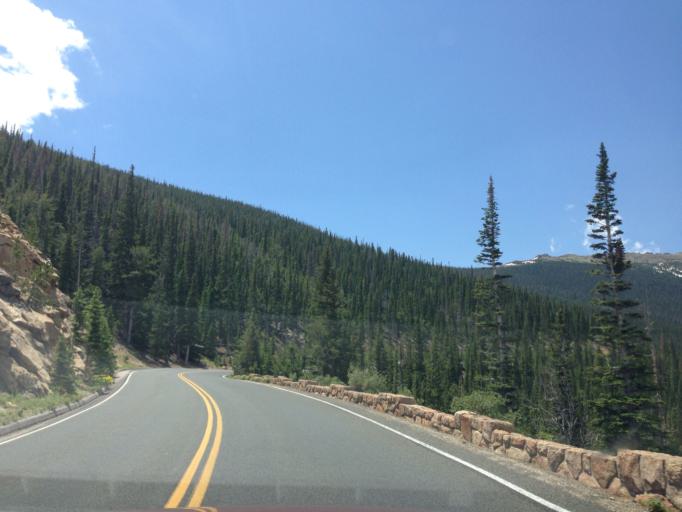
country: US
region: Colorado
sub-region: Larimer County
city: Estes Park
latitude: 40.3924
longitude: -105.6484
